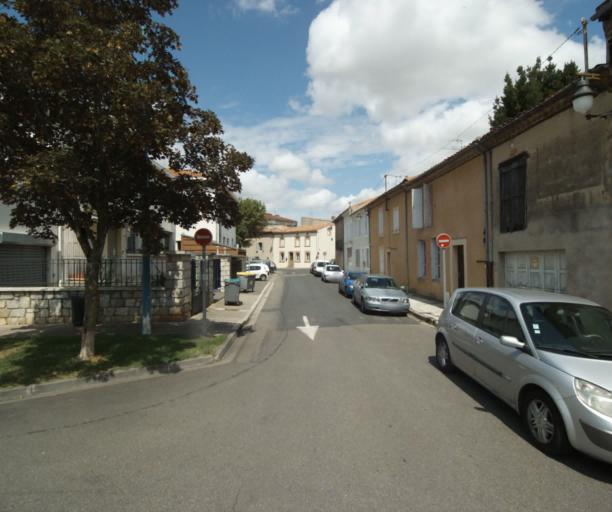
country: FR
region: Midi-Pyrenees
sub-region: Departement de la Haute-Garonne
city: Revel
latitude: 43.4579
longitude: 2.0021
